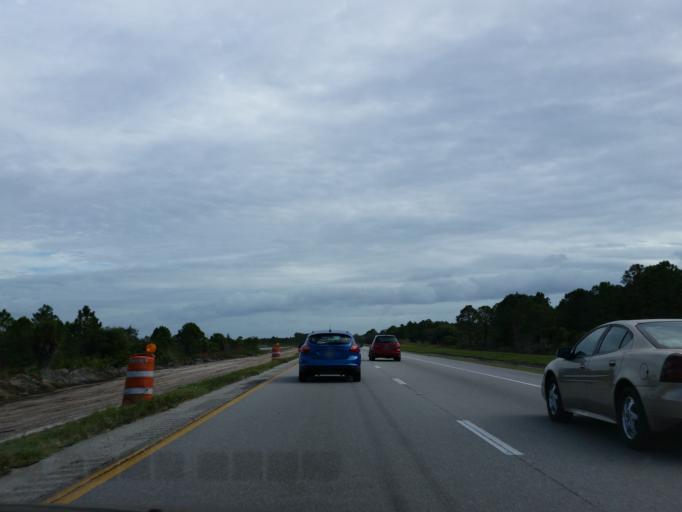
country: US
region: Florida
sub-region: Sarasota County
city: Warm Mineral Springs
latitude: 27.1090
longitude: -82.3097
